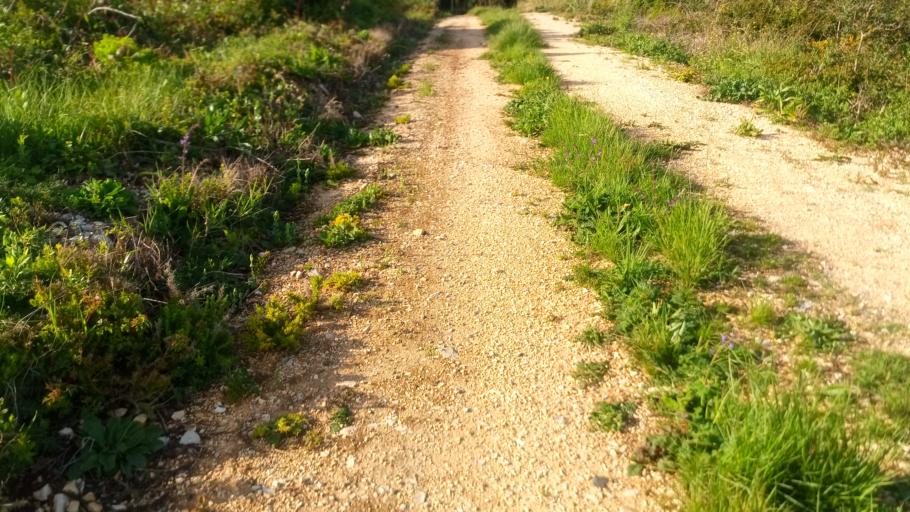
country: PT
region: Leiria
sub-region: Caldas da Rainha
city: Caldas da Rainha
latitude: 39.4562
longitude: -9.1958
